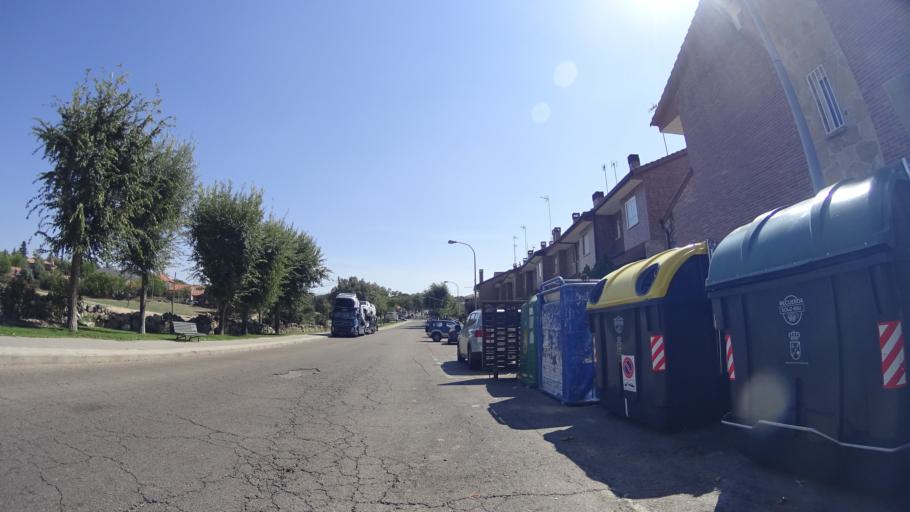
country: ES
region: Madrid
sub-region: Provincia de Madrid
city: Colmenarejo
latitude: 40.5638
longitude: -4.0163
